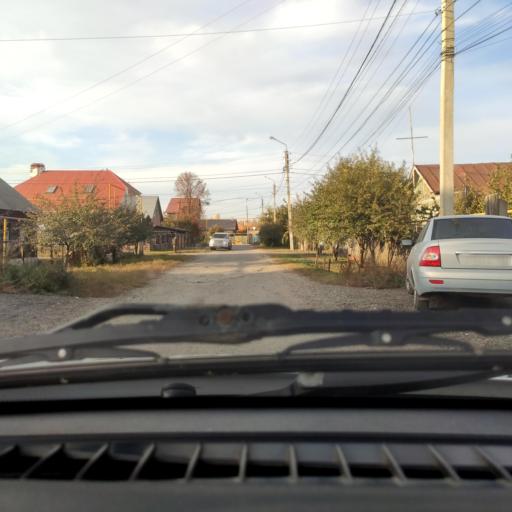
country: RU
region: Samara
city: Tol'yatti
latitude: 53.5265
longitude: 49.4104
